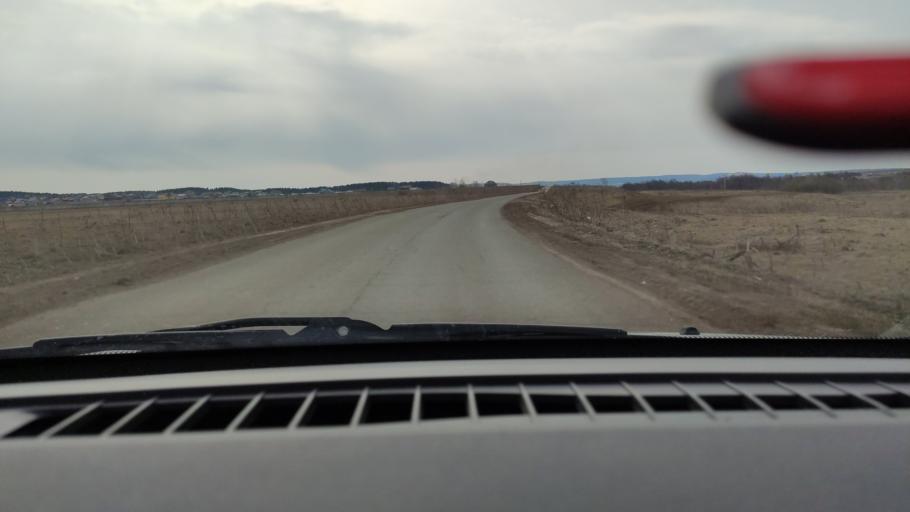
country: RU
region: Perm
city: Kultayevo
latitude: 57.9057
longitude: 55.9912
